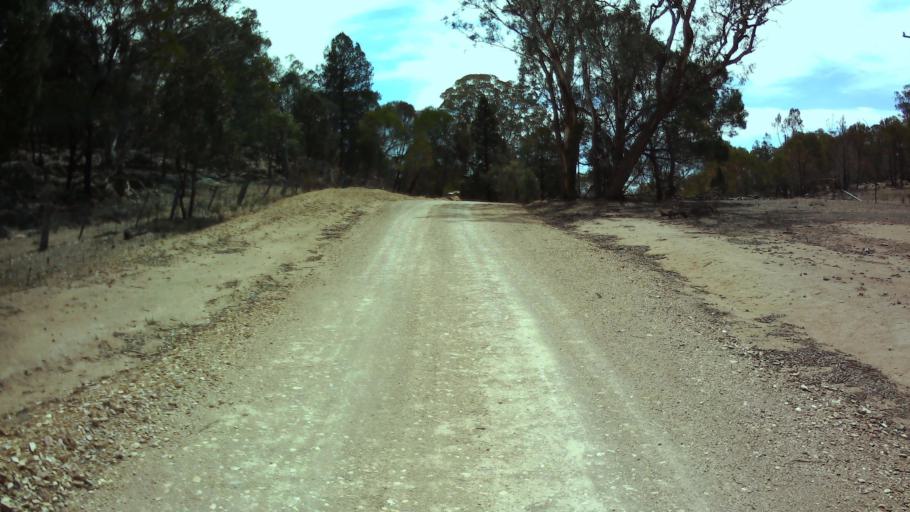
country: AU
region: New South Wales
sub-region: Weddin
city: Grenfell
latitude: -33.7452
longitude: 148.1820
